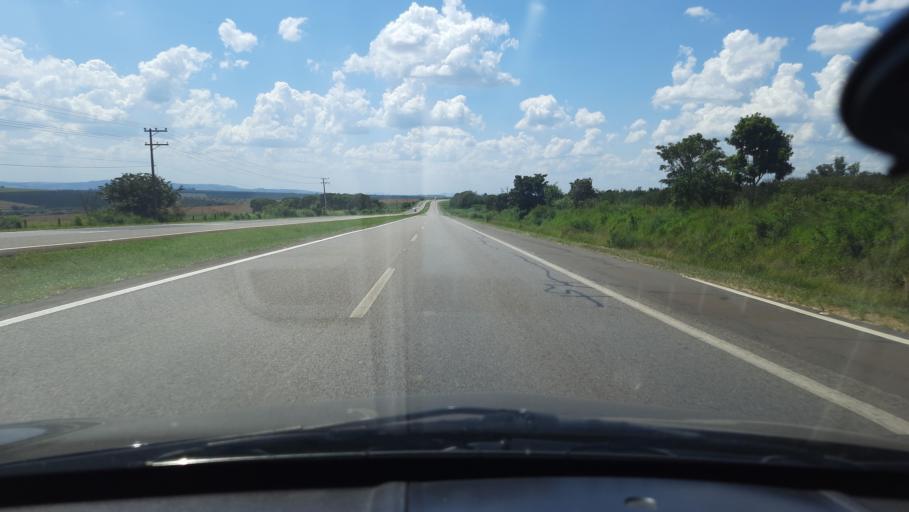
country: BR
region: Sao Paulo
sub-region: Casa Branca
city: Casa Branca
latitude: -21.7177
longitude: -47.0815
